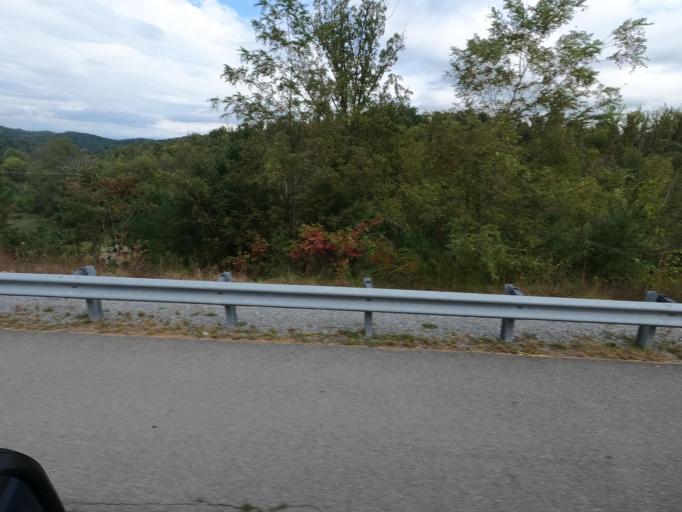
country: US
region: Tennessee
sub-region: Carter County
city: Central
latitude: 36.3076
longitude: -82.2466
